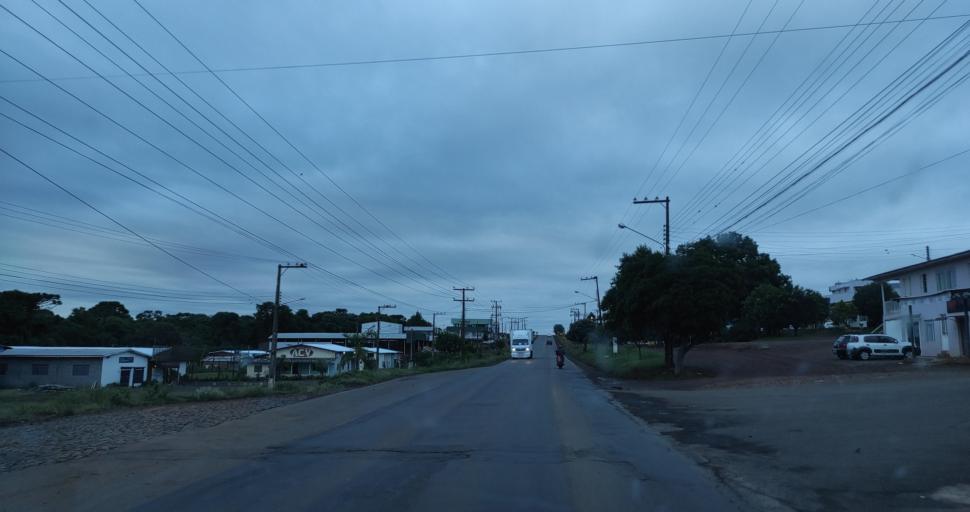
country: BR
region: Santa Catarina
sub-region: Xanxere
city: Xanxere
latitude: -26.7373
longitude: -52.3933
